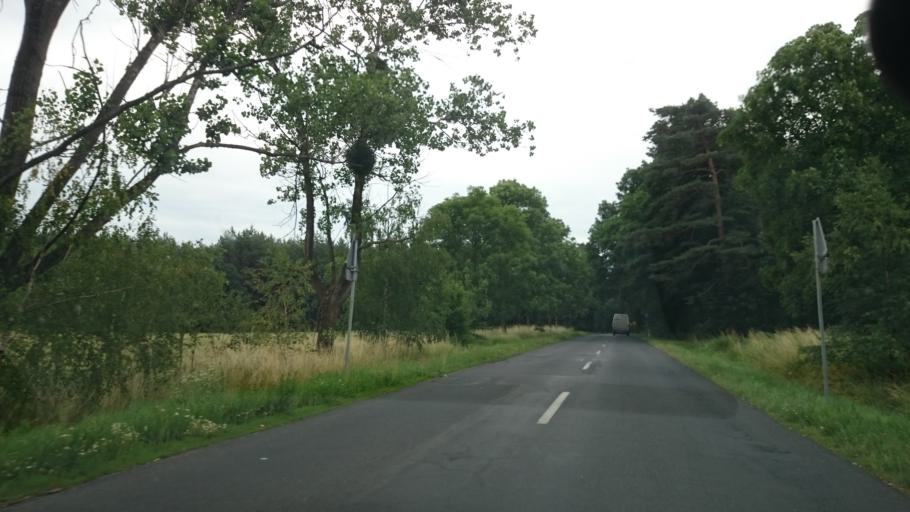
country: PL
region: Opole Voivodeship
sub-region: Powiat opolski
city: Niemodlin
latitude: 50.6290
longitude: 17.5311
